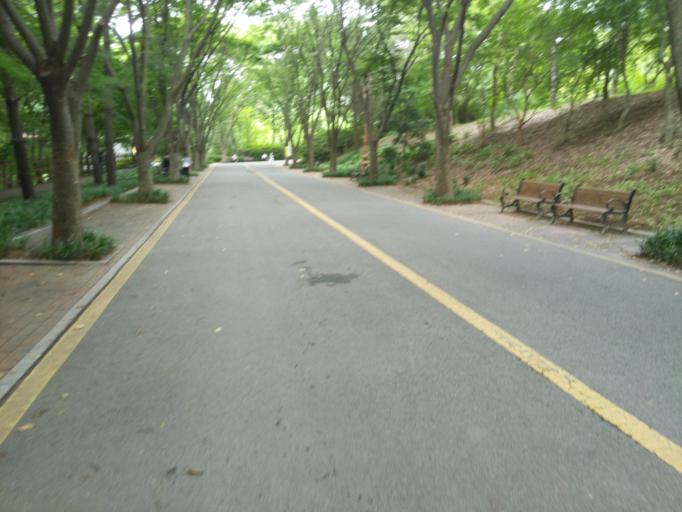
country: KR
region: Daegu
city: Hwawon
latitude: 35.8010
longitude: 128.5219
